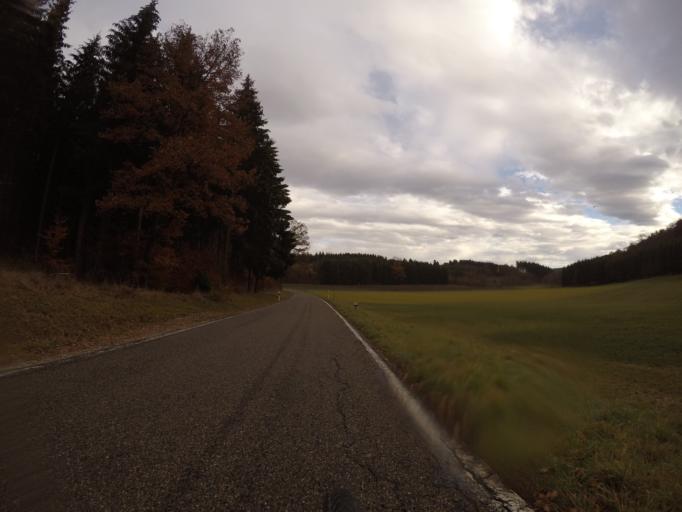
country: DE
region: Baden-Wuerttemberg
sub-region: Tuebingen Region
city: Sankt Johann
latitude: 48.4089
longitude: 9.3016
